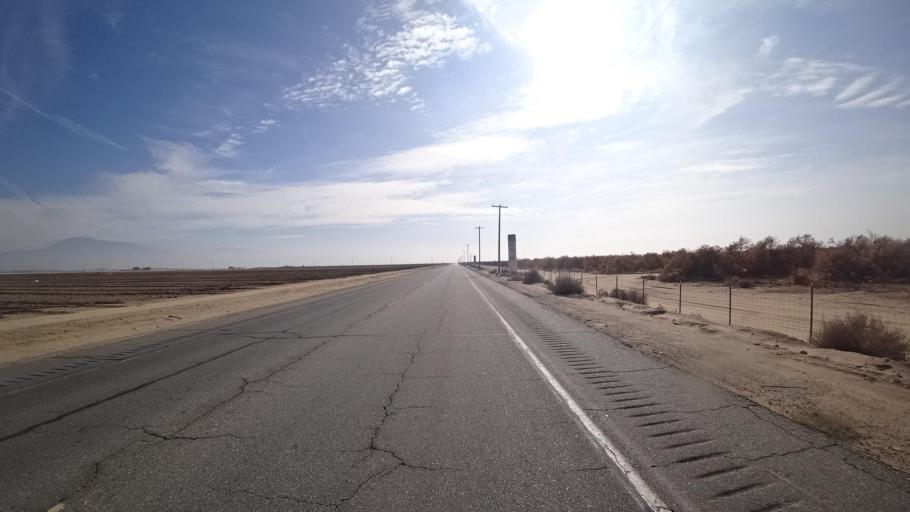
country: US
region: California
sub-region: Kern County
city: Lamont
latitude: 35.3338
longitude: -118.8432
